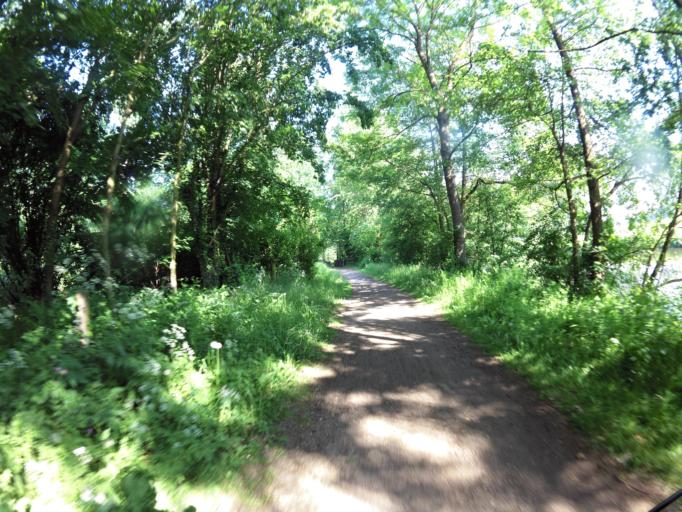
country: DE
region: North Rhine-Westphalia
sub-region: Regierungsbezirk Koln
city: Linnich
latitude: 50.9641
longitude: 6.2836
